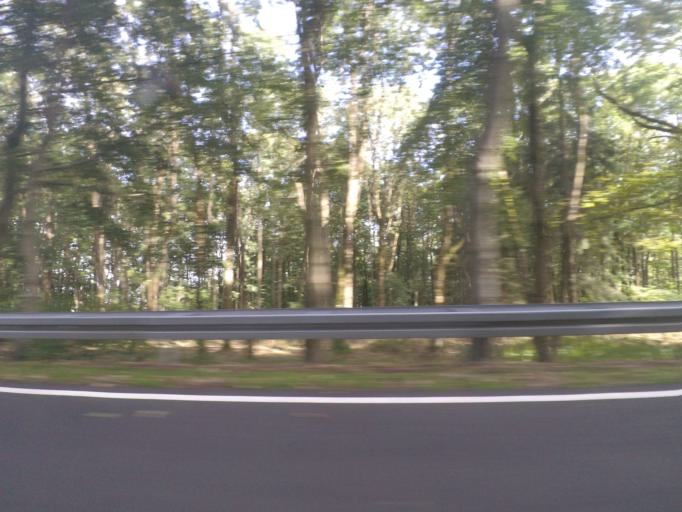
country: DE
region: Thuringia
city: Stepfershausen
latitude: 50.5799
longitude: 10.2757
